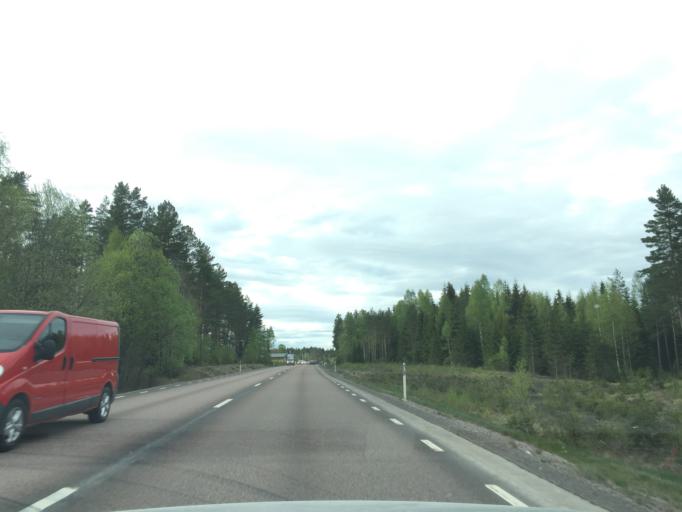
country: SE
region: Vaermland
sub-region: Eda Kommun
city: Charlottenberg
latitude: 59.8876
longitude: 12.2821
